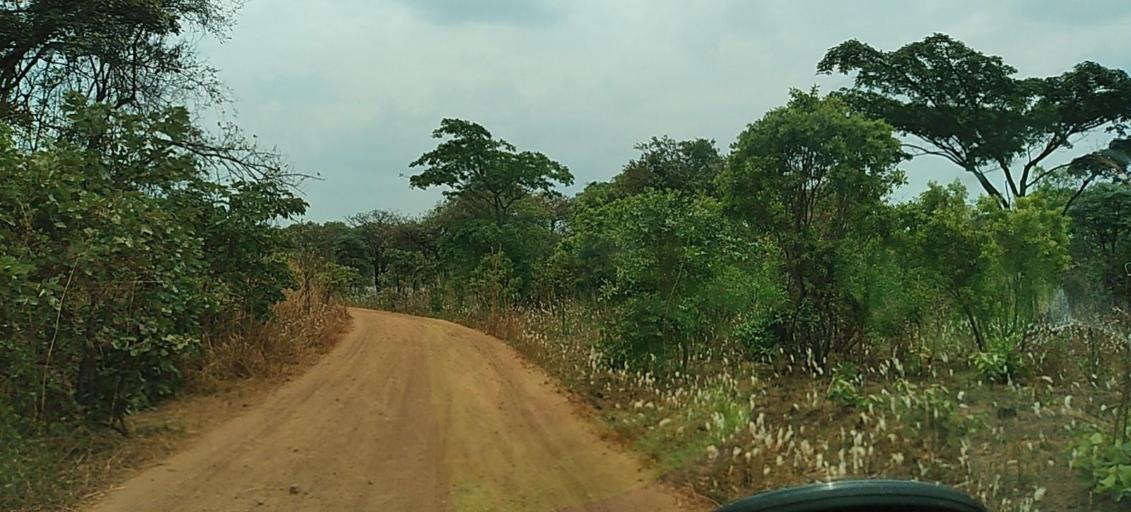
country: ZM
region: North-Western
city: Kansanshi
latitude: -12.0605
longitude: 26.3504
